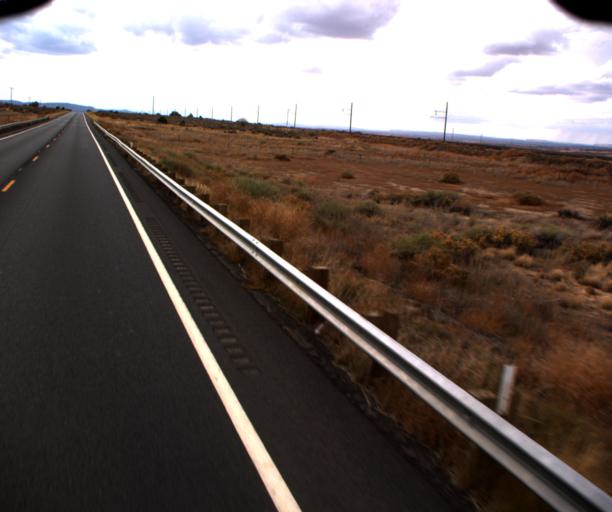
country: US
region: Arizona
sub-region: Navajo County
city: Kayenta
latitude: 36.5158
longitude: -110.5951
